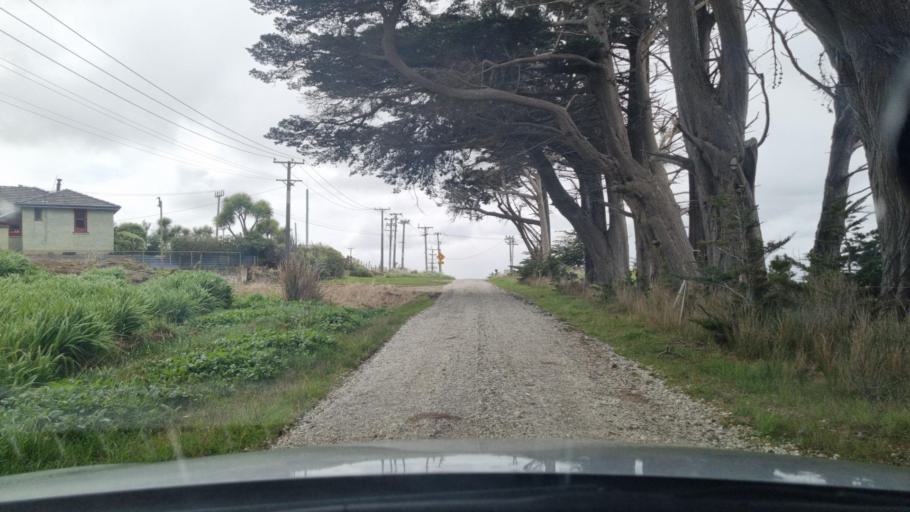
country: NZ
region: Southland
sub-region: Invercargill City
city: Bluff
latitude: -46.5859
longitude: 168.3033
